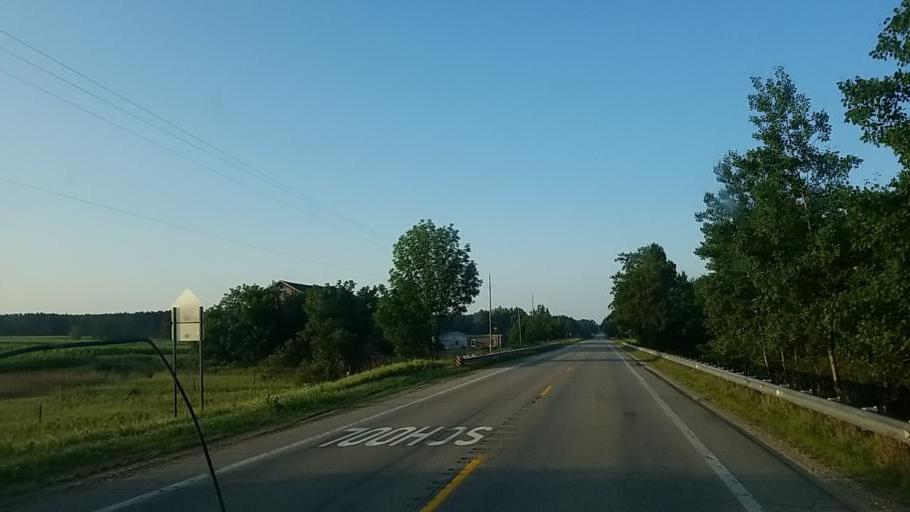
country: US
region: Michigan
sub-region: Isabella County
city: Lake Isabella
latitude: 43.6577
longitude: -85.1463
